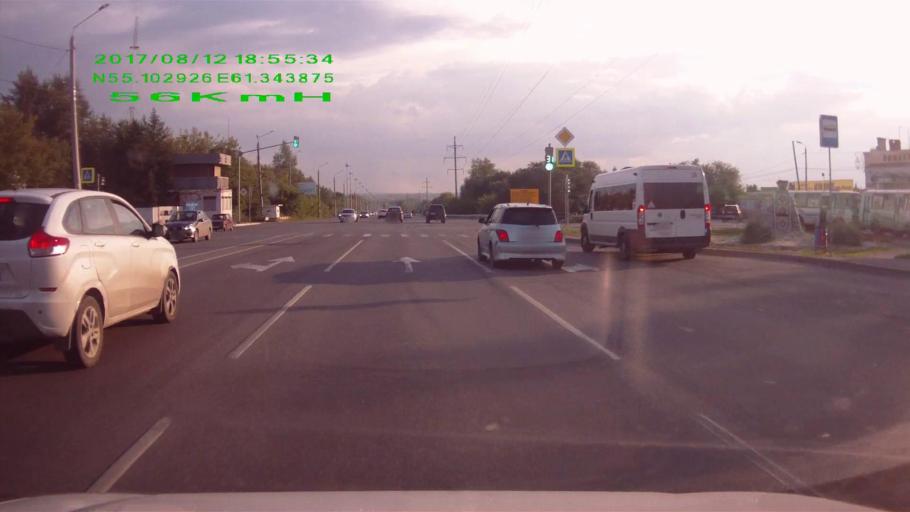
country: RU
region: Chelyabinsk
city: Novosineglazovskiy
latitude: 55.0968
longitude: 61.3355
